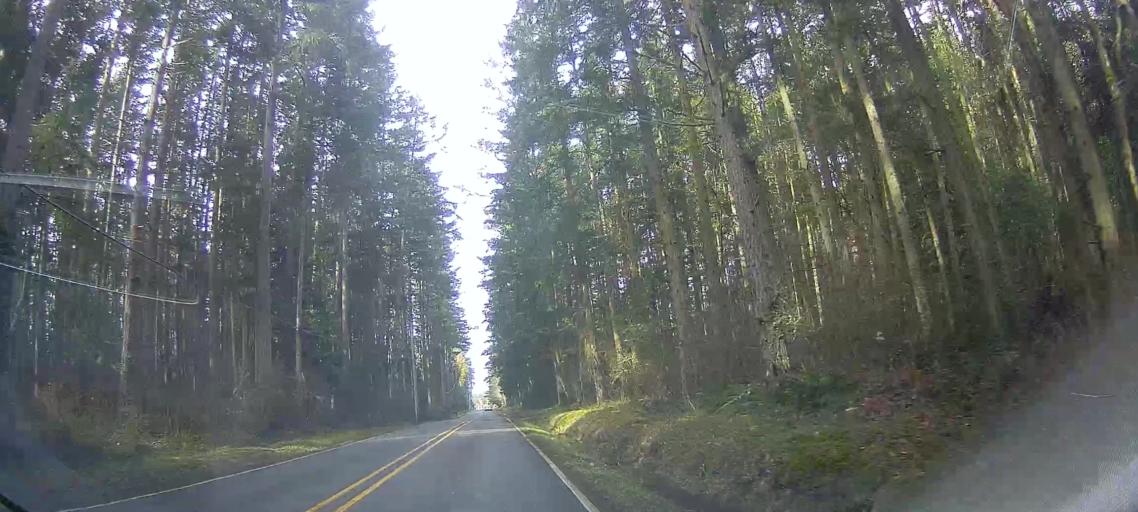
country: US
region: Washington
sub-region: Island County
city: Camano
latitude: 48.1513
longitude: -122.5128
